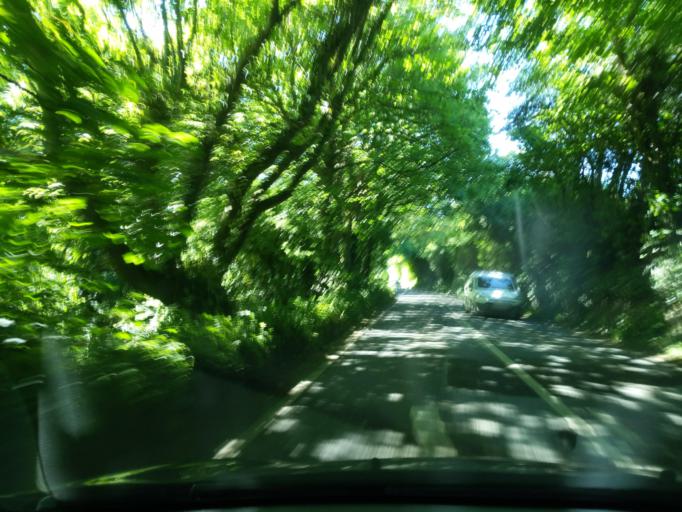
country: GB
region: England
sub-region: Cornwall
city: Porthleven
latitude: 50.1052
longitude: -5.3307
